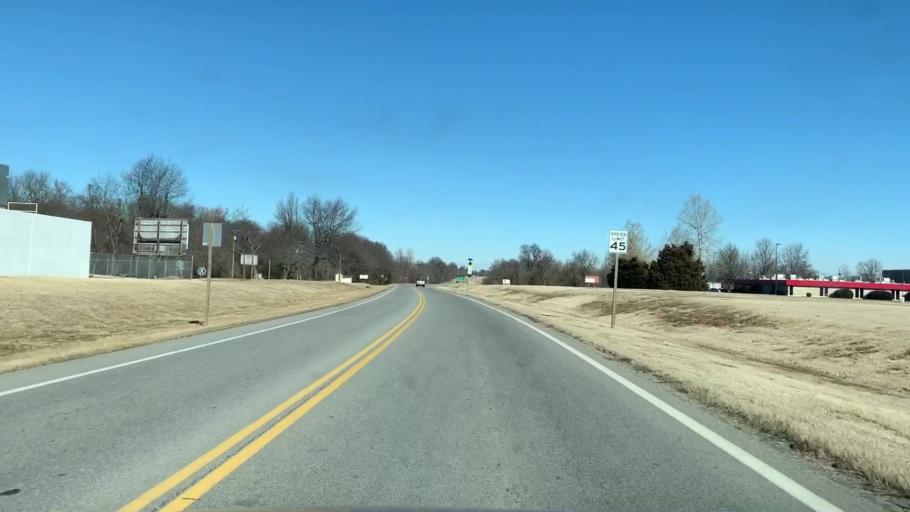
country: US
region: Kansas
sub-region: Cherokee County
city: Baxter Springs
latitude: 37.0353
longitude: -94.7347
